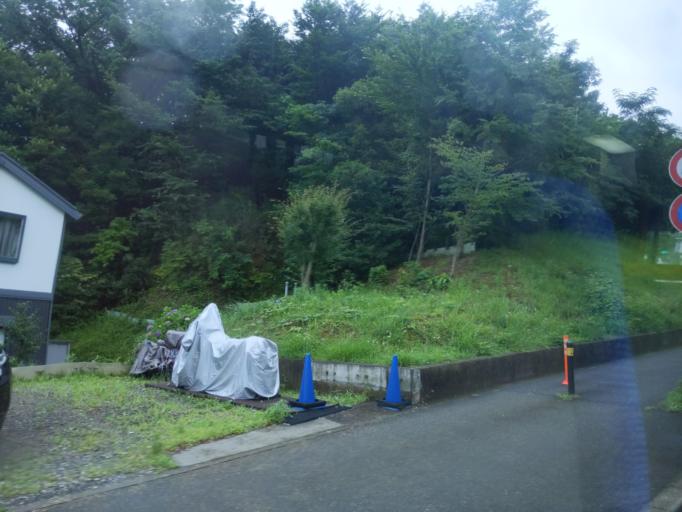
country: JP
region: Tokyo
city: Chofugaoka
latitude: 35.6082
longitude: 139.5642
